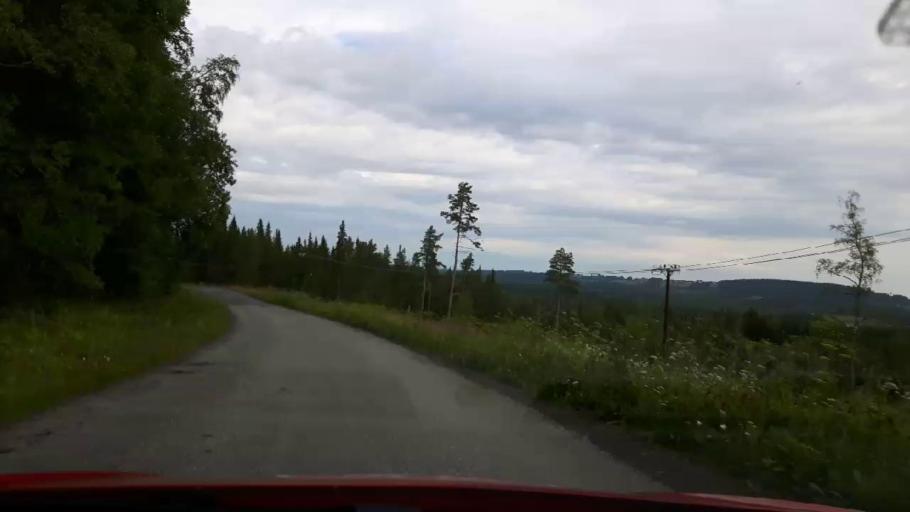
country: SE
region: Jaemtland
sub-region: Stroemsunds Kommun
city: Stroemsund
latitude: 63.5278
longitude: 15.3594
